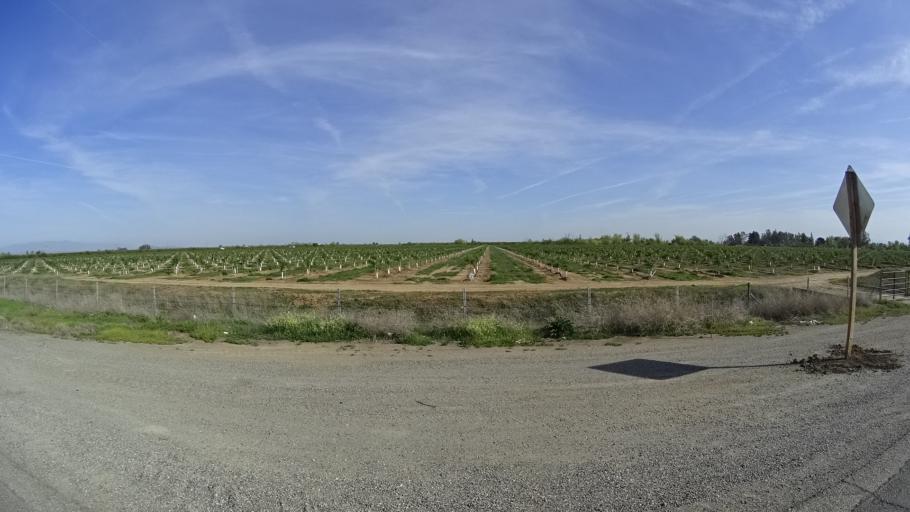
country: US
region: California
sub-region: Glenn County
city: Willows
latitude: 39.6241
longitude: -122.2030
